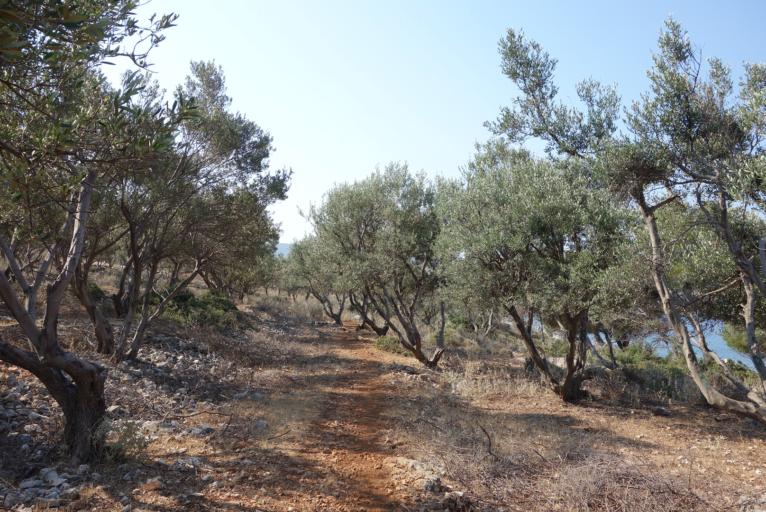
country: AL
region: Vlore
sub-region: Rrethi i Sarandes
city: Xarre
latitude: 39.7856
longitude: 20.0061
